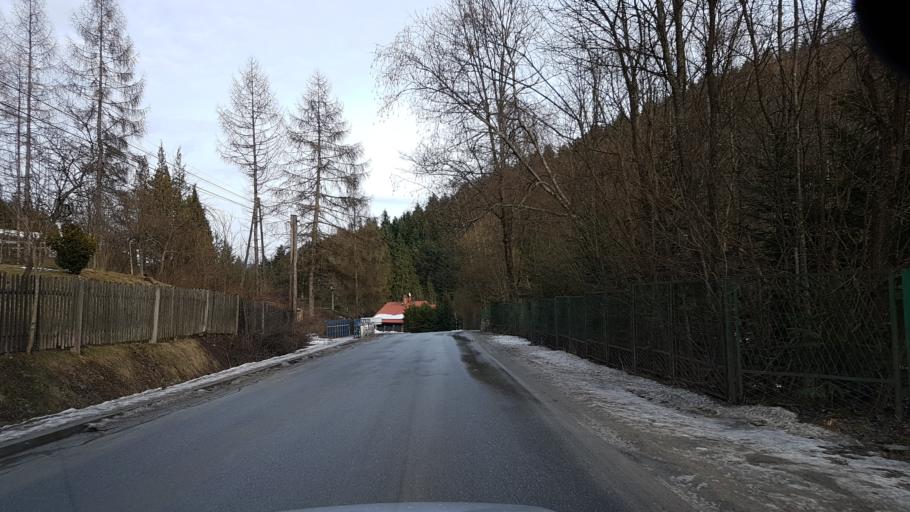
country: PL
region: Lesser Poland Voivodeship
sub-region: Powiat nowosadecki
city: Piwniczna-Zdroj
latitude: 49.4314
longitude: 20.6770
